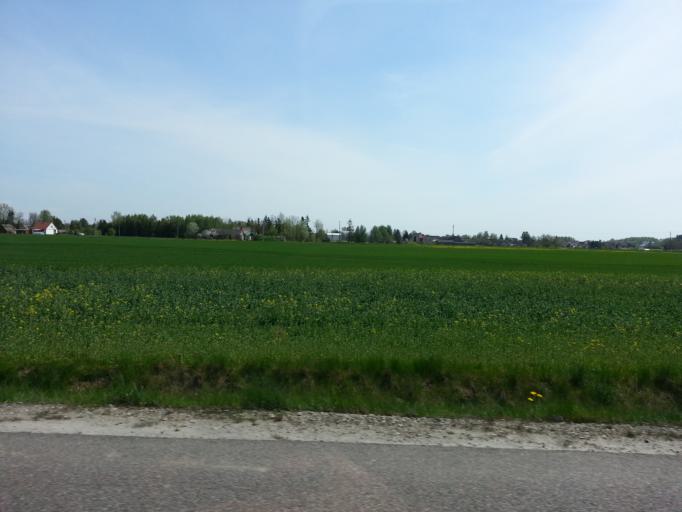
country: LT
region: Panevezys
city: Pasvalys
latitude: 55.9780
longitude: 24.3417
